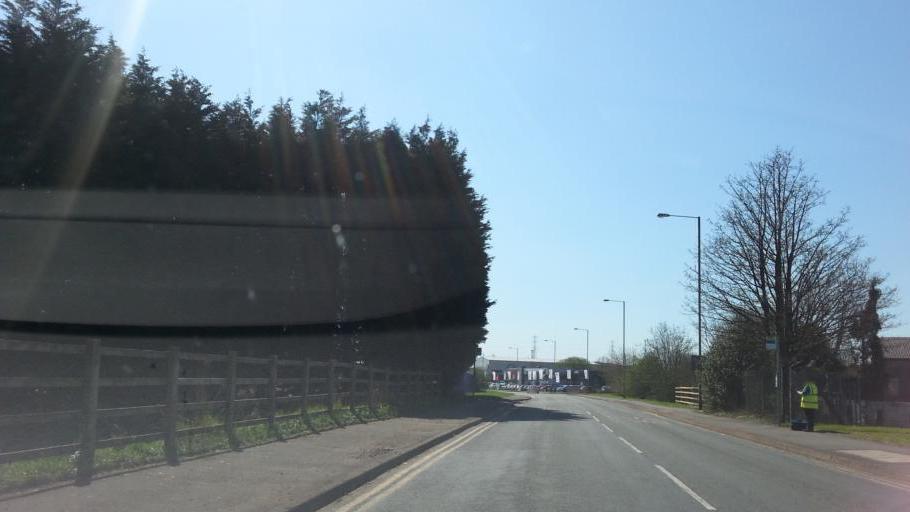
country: GB
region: England
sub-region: Staffordshire
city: Cannock
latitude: 52.6781
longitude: -2.0335
